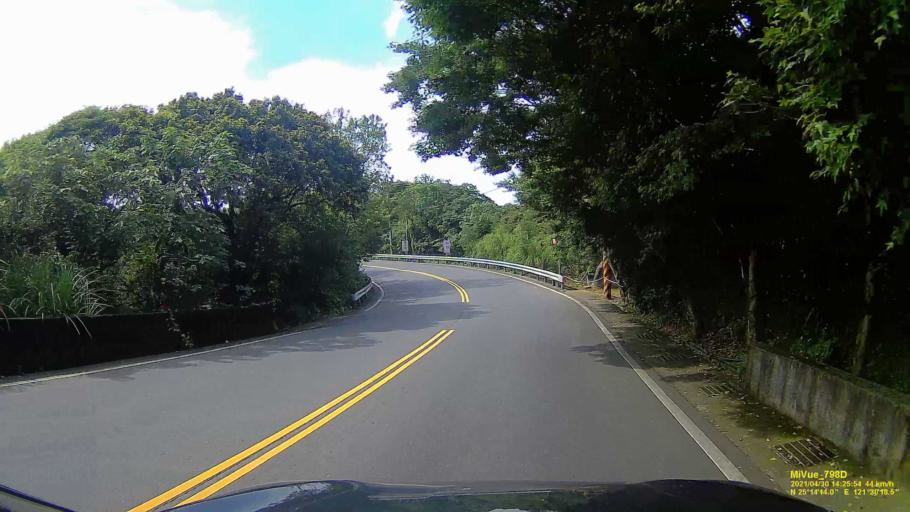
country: TW
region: Taipei
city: Taipei
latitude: 25.2375
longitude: 121.5050
